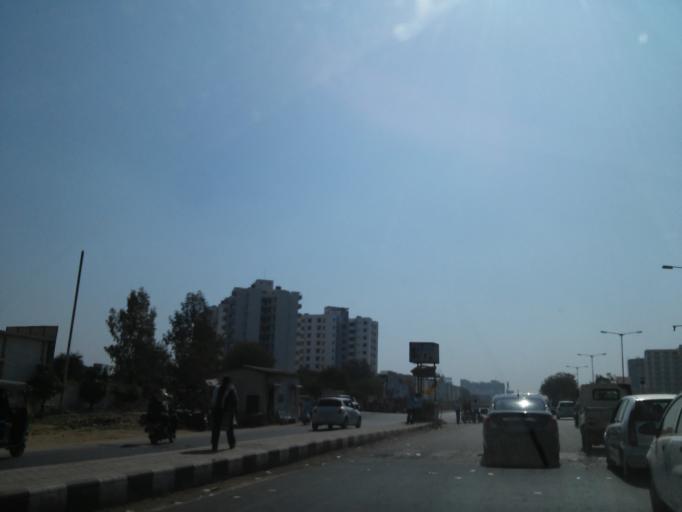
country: IN
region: Gujarat
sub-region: Ahmadabad
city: Ahmedabad
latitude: 23.0888
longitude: 72.5289
